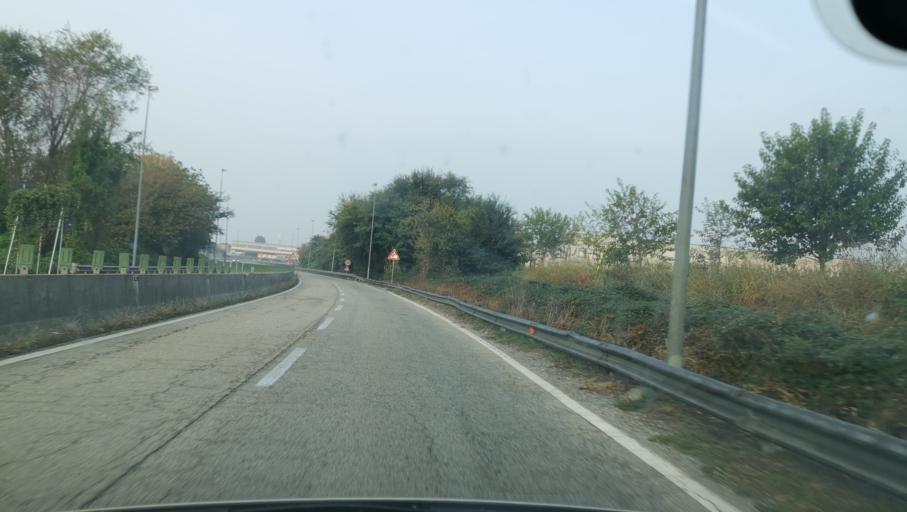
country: IT
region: Piedmont
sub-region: Provincia di Torino
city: San Mauro Torinese
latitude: 45.1129
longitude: 7.7410
